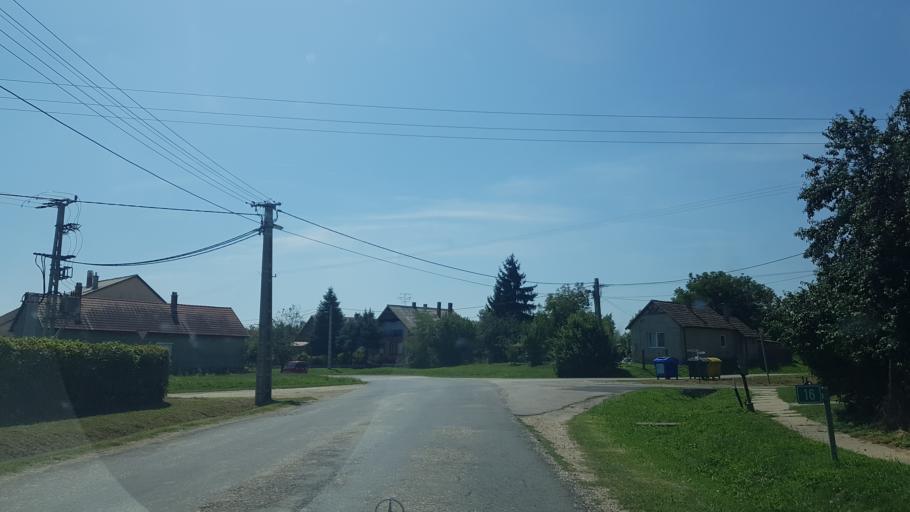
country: HU
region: Somogy
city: Segesd
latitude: 46.3382
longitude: 17.3416
